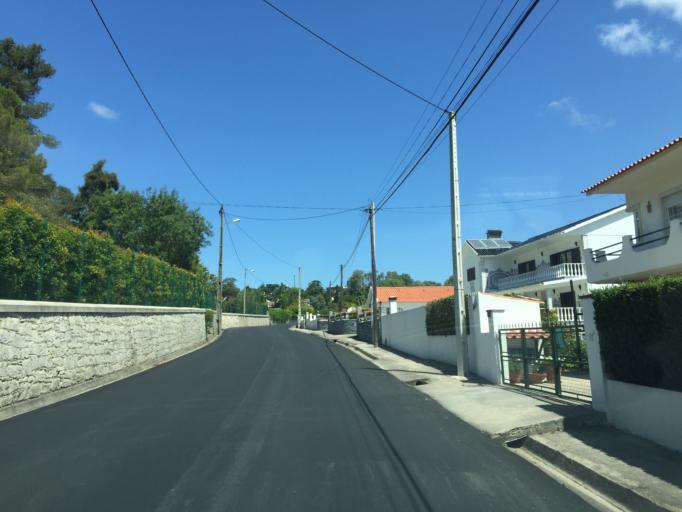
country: PT
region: Lisbon
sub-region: Sintra
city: Sintra
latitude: 38.8092
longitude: -9.4019
